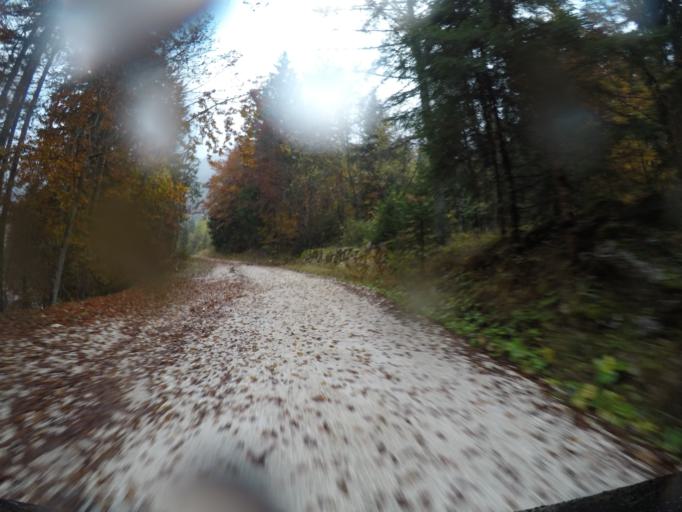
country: SI
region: Kranjska Gora
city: Kranjska Gora
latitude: 46.4042
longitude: 13.7110
